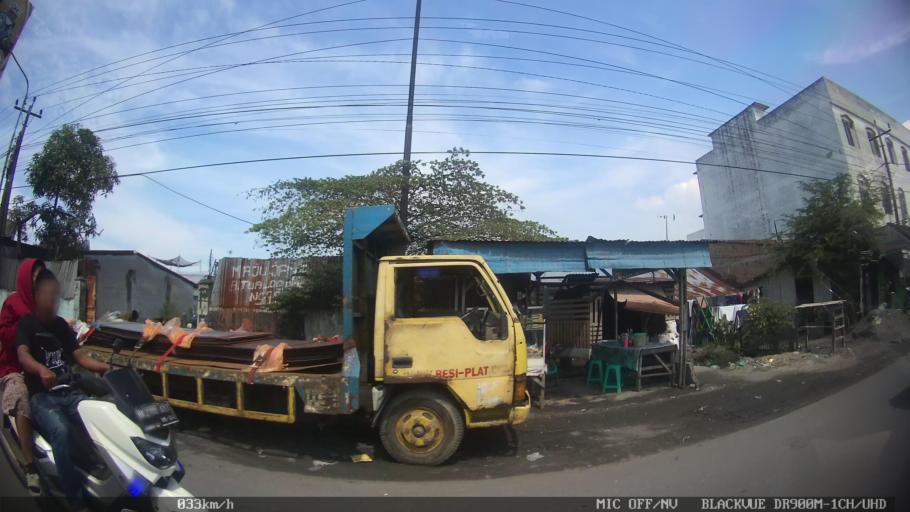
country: ID
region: North Sumatra
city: Labuhan Deli
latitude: 3.6641
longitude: 98.6563
